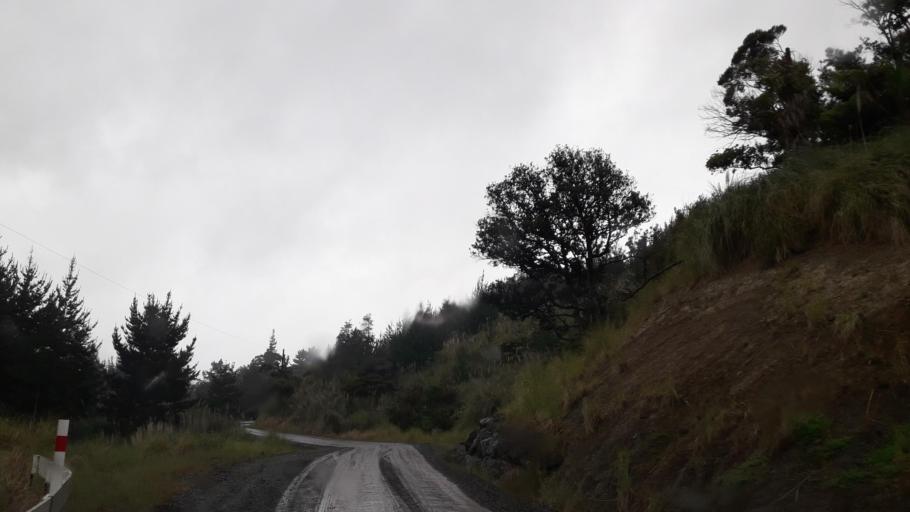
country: NZ
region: Northland
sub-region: Far North District
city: Kaitaia
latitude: -35.3725
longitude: 173.4112
